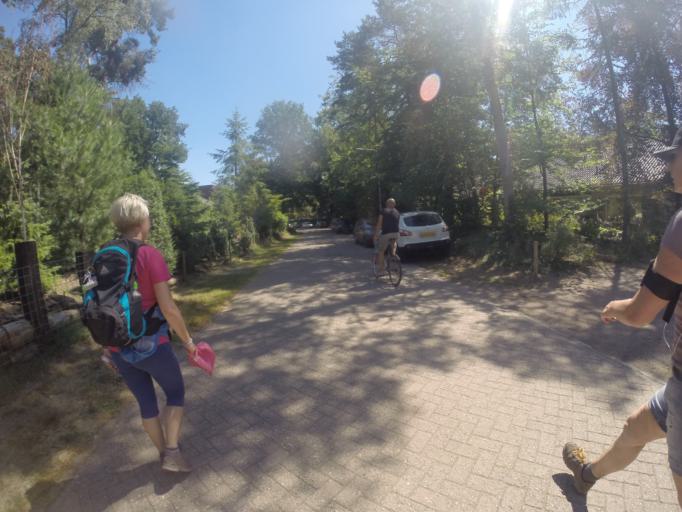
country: NL
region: Gelderland
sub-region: Gemeente Lochem
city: Barchem
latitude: 52.1252
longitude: 6.4390
